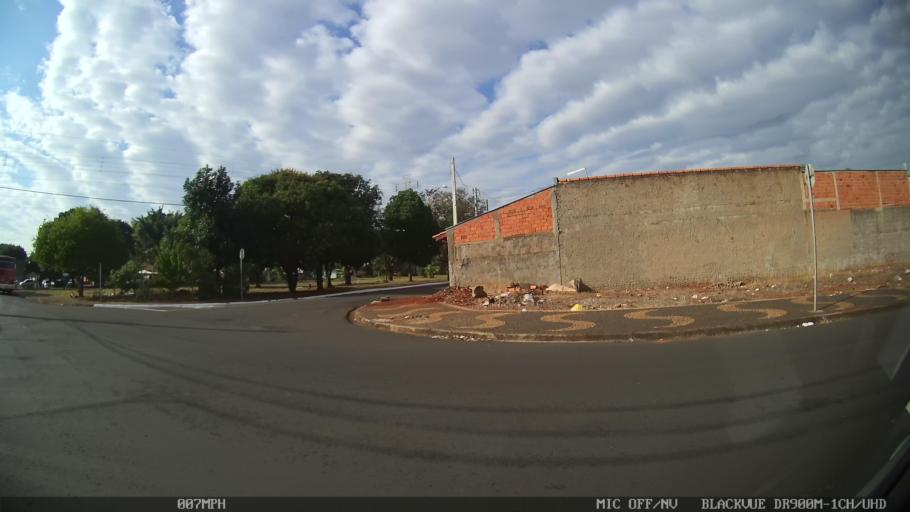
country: BR
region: Sao Paulo
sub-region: Americana
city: Americana
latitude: -22.7332
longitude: -47.3603
